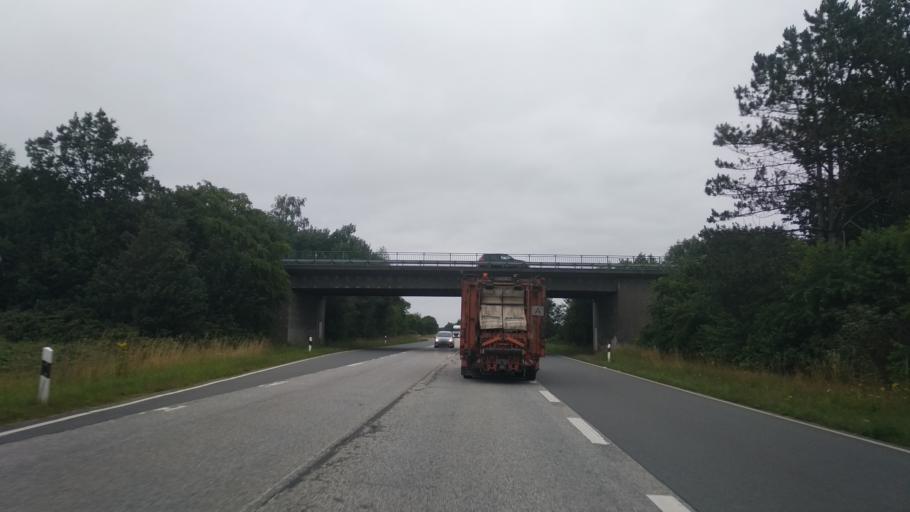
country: DE
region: Schleswig-Holstein
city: Lurschau
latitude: 54.5756
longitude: 9.4800
